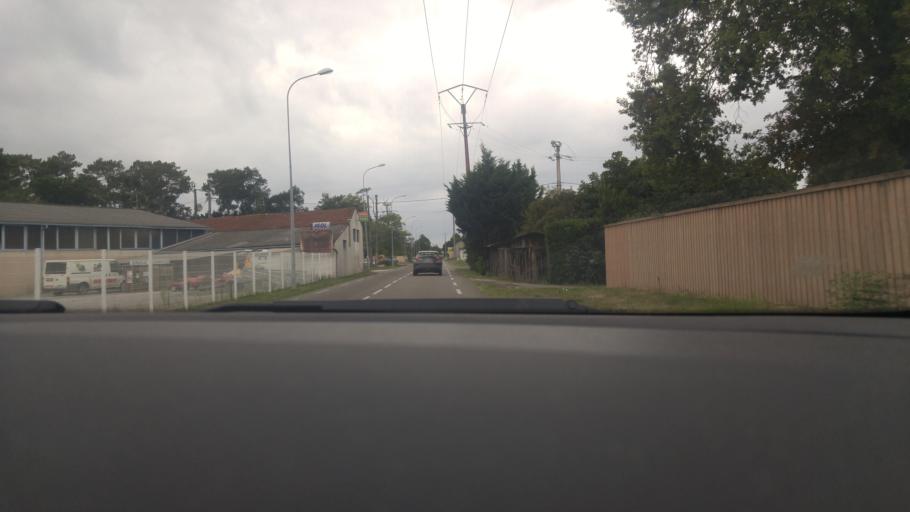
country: FR
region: Aquitaine
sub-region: Departement des Landes
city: Soustons
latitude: 43.7472
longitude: -1.3223
